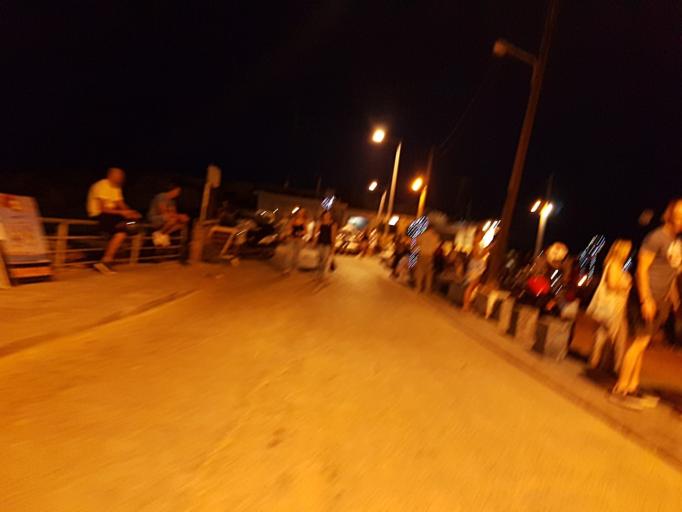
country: GR
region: Crete
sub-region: Nomos Irakleiou
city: Limin Khersonisou
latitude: 35.3228
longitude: 25.3916
